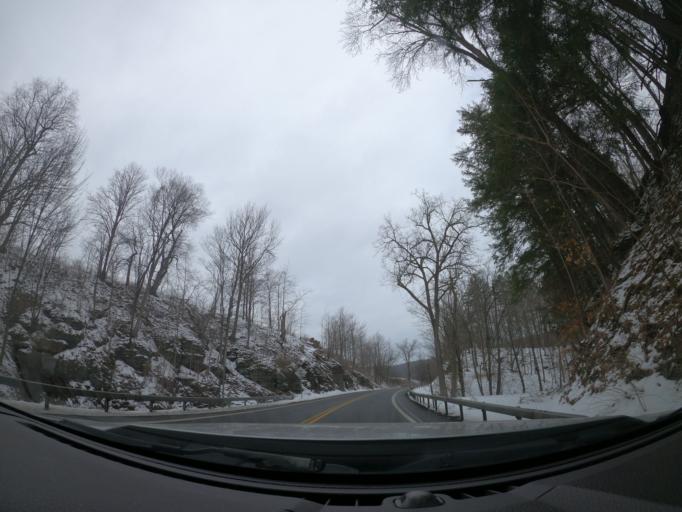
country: US
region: New York
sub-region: Cortland County
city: Homer
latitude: 42.6705
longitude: -76.2209
